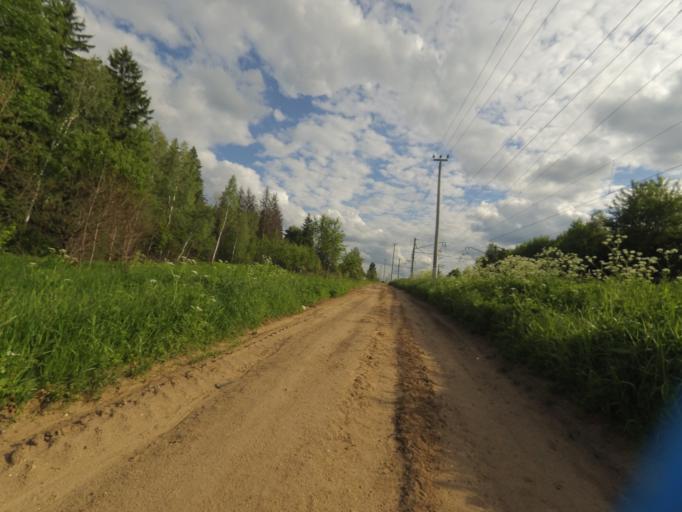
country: RU
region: Moskovskaya
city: Nekrasovskiy
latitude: 56.0996
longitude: 37.5090
